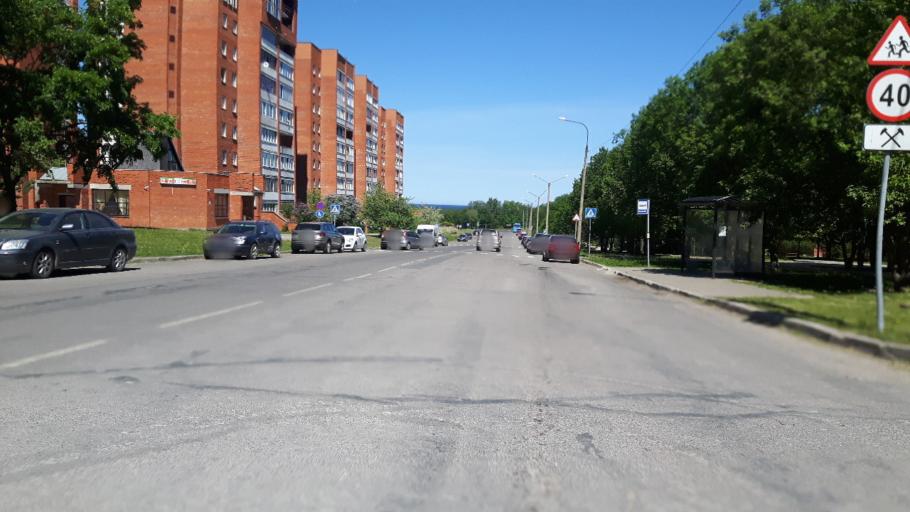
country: EE
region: Ida-Virumaa
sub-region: Sillamaee linn
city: Sillamae
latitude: 59.3915
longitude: 27.7969
